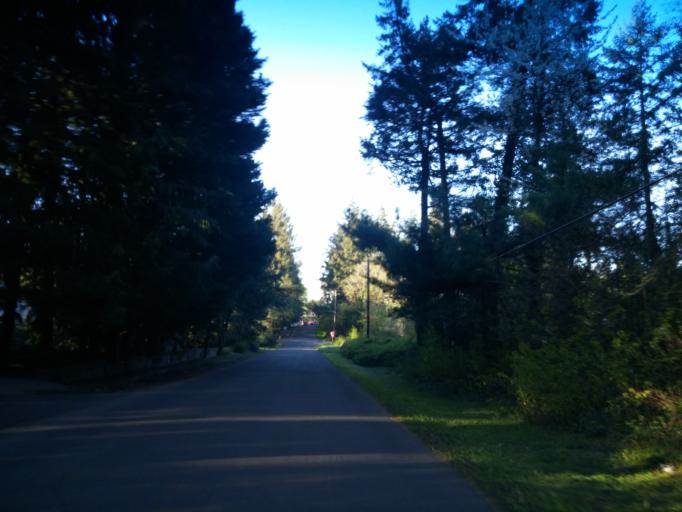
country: US
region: Oregon
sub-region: Washington County
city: Cedar Hills
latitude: 45.5028
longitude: -122.7944
